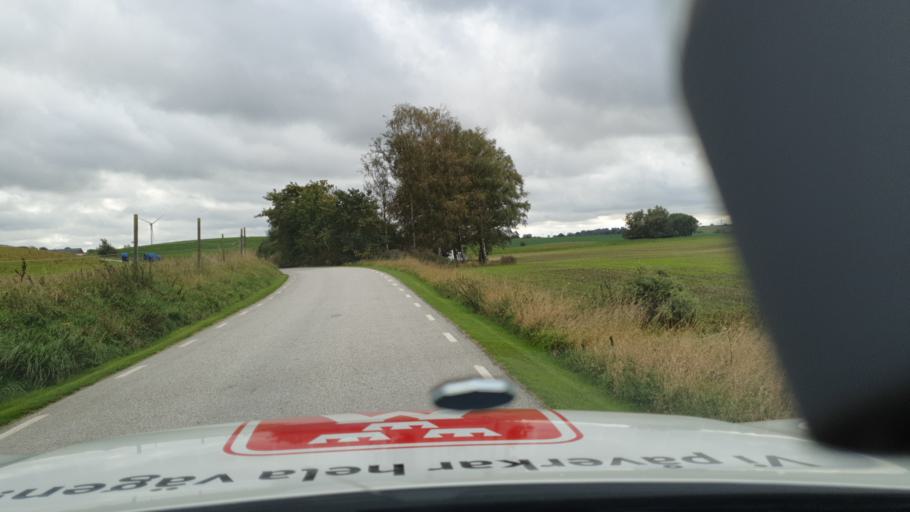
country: SE
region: Skane
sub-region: Svedala Kommun
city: Svedala
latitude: 55.4949
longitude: 13.1856
